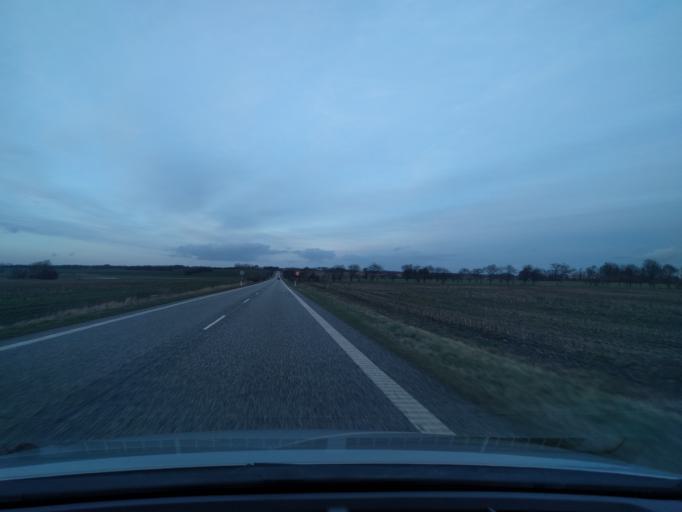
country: DK
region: South Denmark
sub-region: Tonder Kommune
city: Logumkloster
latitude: 55.1241
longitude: 8.9755
